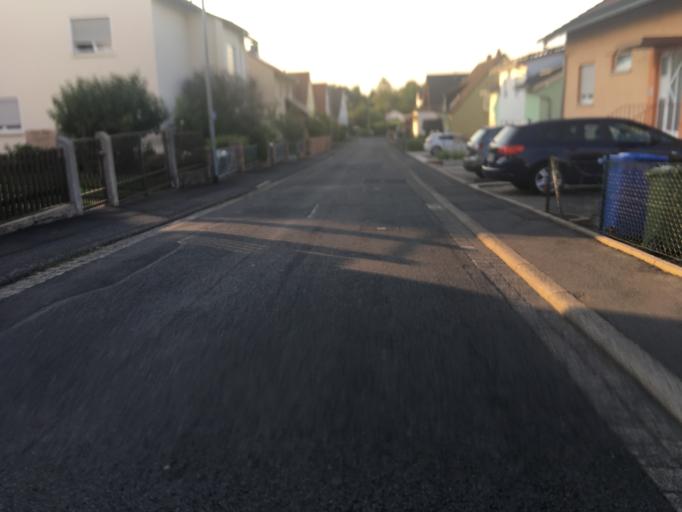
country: DE
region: Hesse
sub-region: Regierungsbezirk Darmstadt
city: Gelnhausen
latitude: 50.1872
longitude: 9.1488
